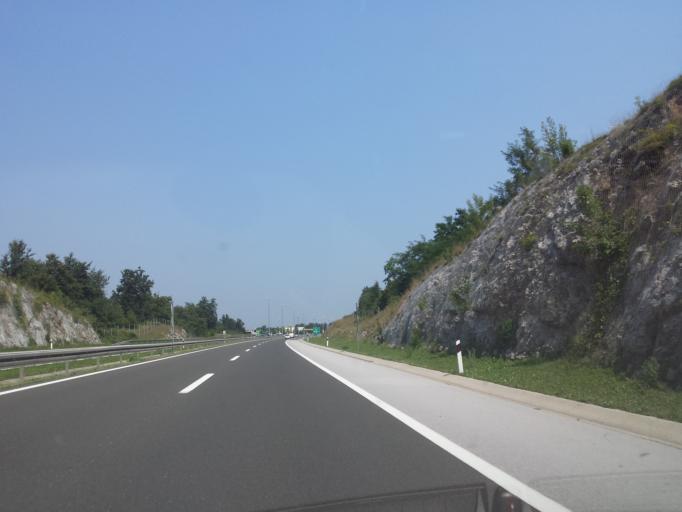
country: HR
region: Karlovacka
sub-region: Grad Ogulin
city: Ogulin
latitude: 45.3034
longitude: 15.2789
